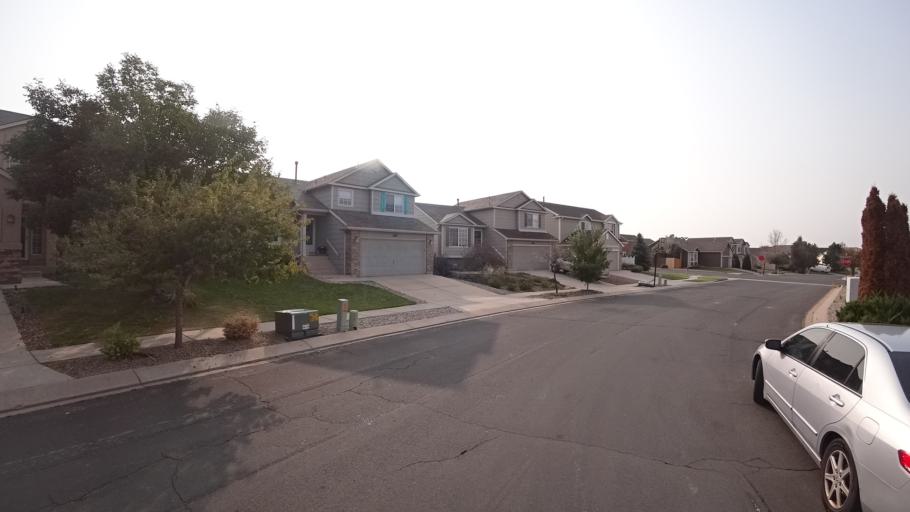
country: US
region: Colorado
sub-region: El Paso County
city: Cimarron Hills
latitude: 38.9353
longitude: -104.7255
